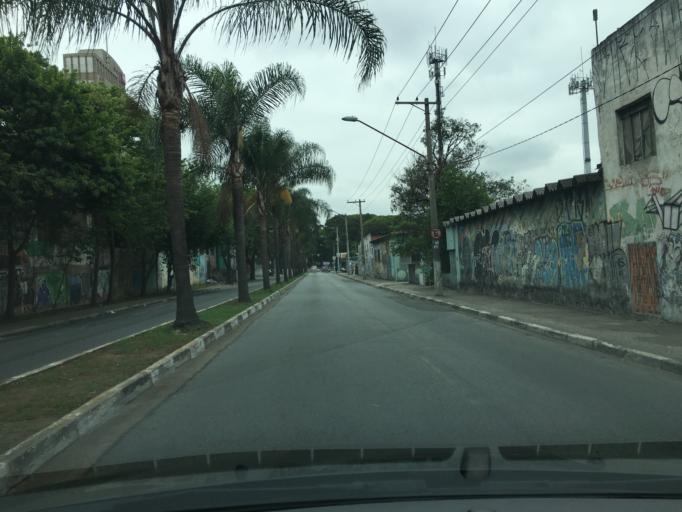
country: BR
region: Sao Paulo
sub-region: Guarulhos
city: Guarulhos
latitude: -23.4751
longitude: -46.5337
